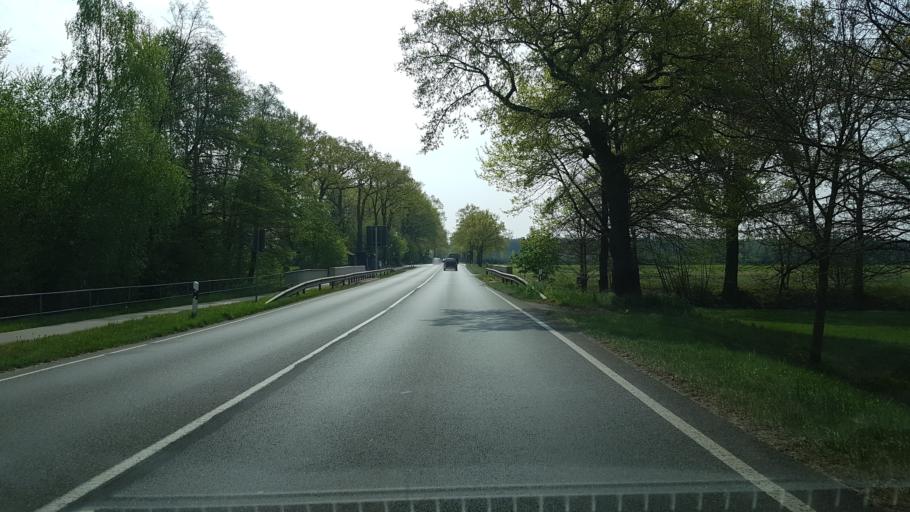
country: DE
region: Lower Saxony
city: Soltau
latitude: 52.9678
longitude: 9.8532
